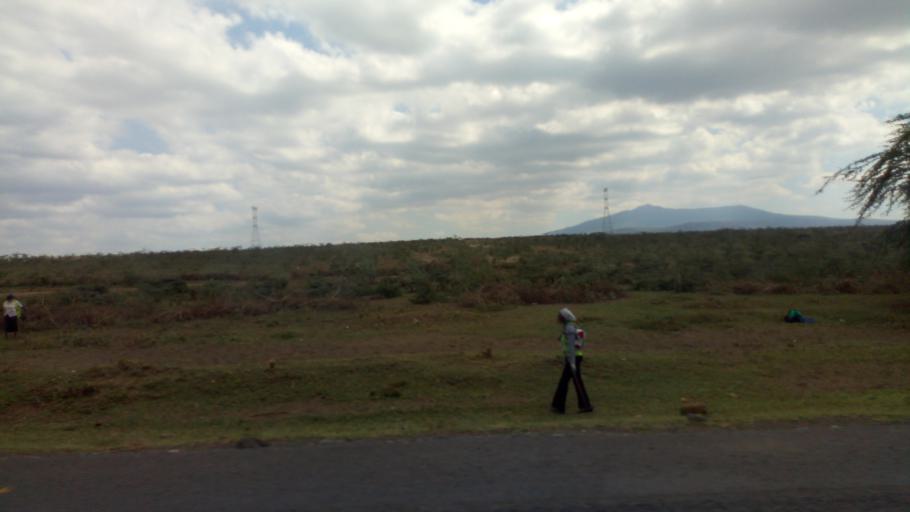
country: KE
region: Nakuru
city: Kijabe
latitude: -1.0307
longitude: 36.4366
